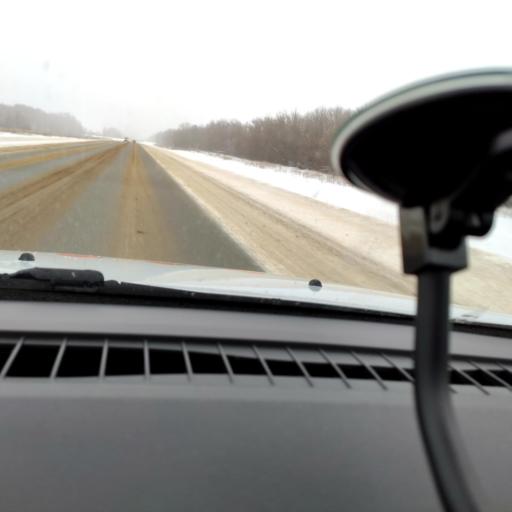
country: RU
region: Samara
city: Dubovyy Umet
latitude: 53.0366
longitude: 50.2128
